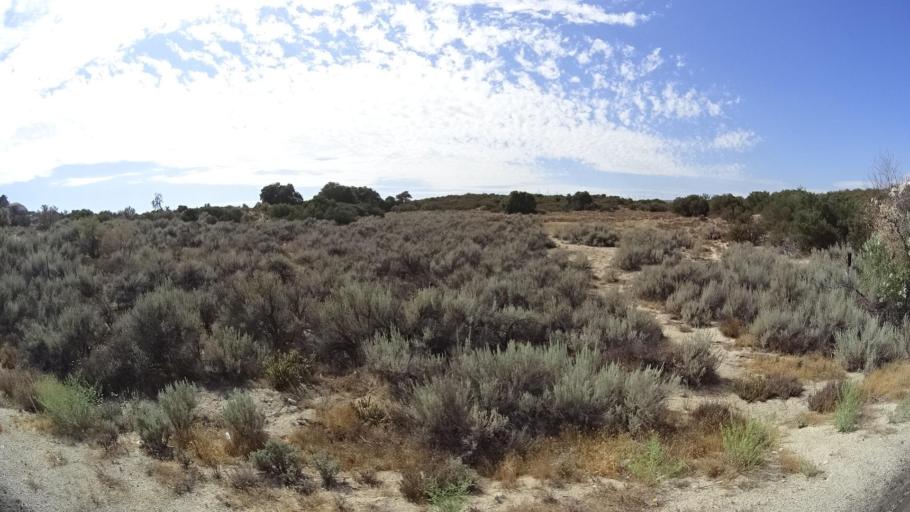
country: US
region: California
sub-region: San Diego County
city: Campo
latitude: 32.6976
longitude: -116.2934
